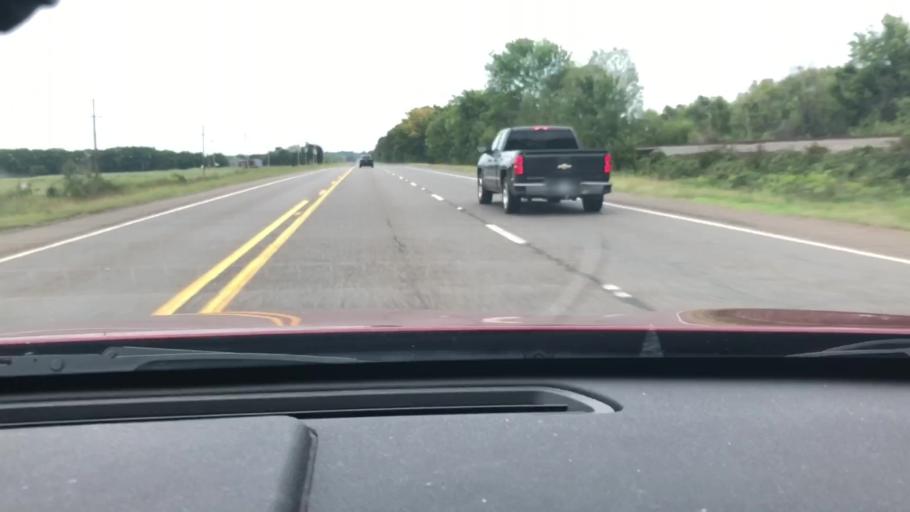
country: US
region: Arkansas
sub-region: Lafayette County
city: Lewisville
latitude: 33.3559
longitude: -93.6581
